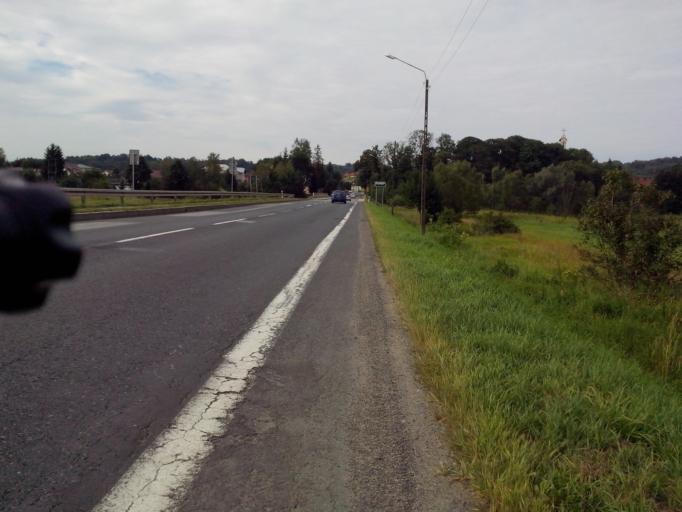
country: PL
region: Subcarpathian Voivodeship
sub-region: Powiat brzozowski
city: Domaradz
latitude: 49.7926
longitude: 21.9472
